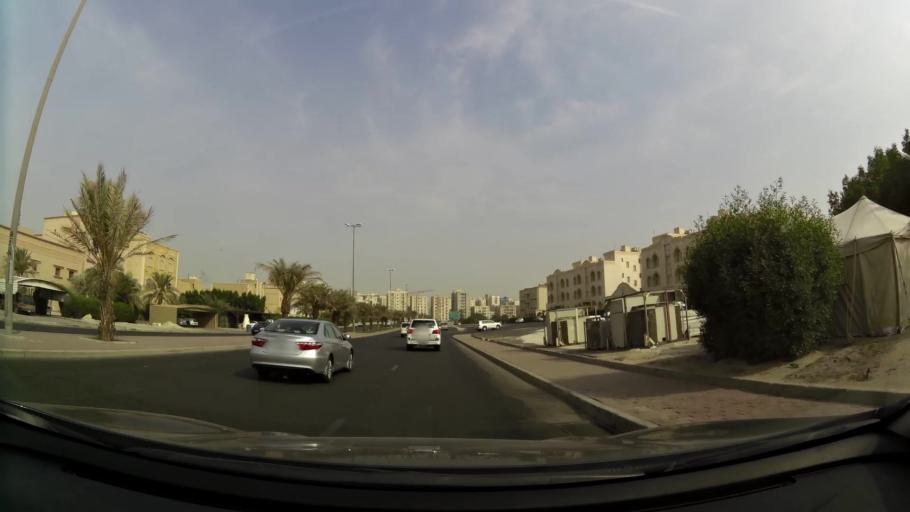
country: KW
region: Al Farwaniyah
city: Al Farwaniyah
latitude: 29.2798
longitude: 47.9449
